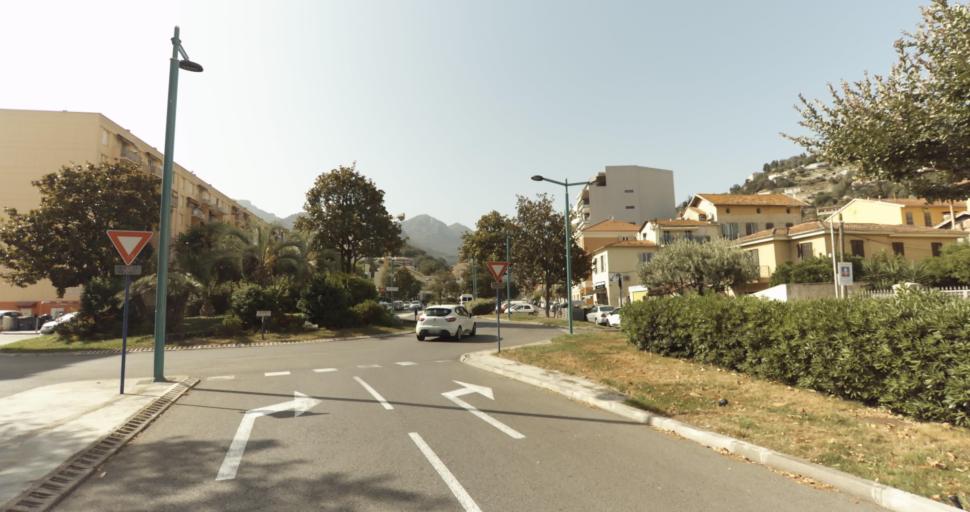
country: FR
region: Provence-Alpes-Cote d'Azur
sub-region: Departement des Alpes-Maritimes
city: Roquebrune-Cap-Martin
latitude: 43.7772
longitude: 7.4874
